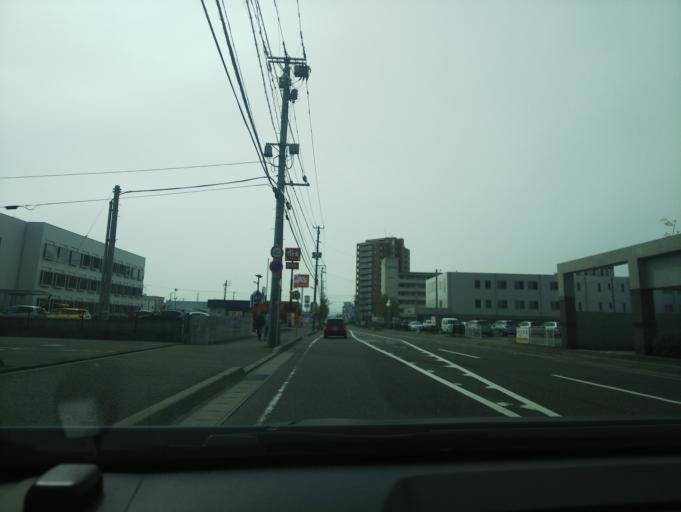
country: JP
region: Niigata
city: Niigata-shi
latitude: 37.9099
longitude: 139.0685
